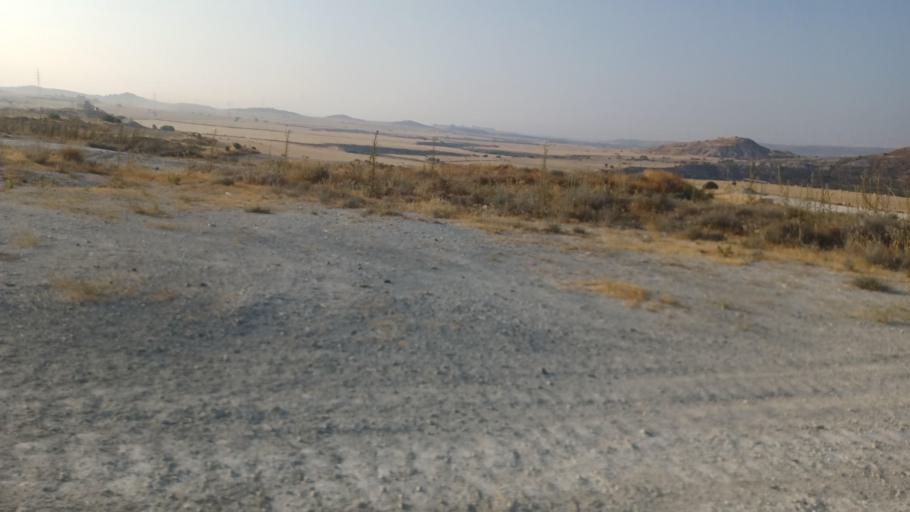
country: CY
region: Larnaka
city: Psevdas
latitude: 34.9212
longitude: 33.5138
